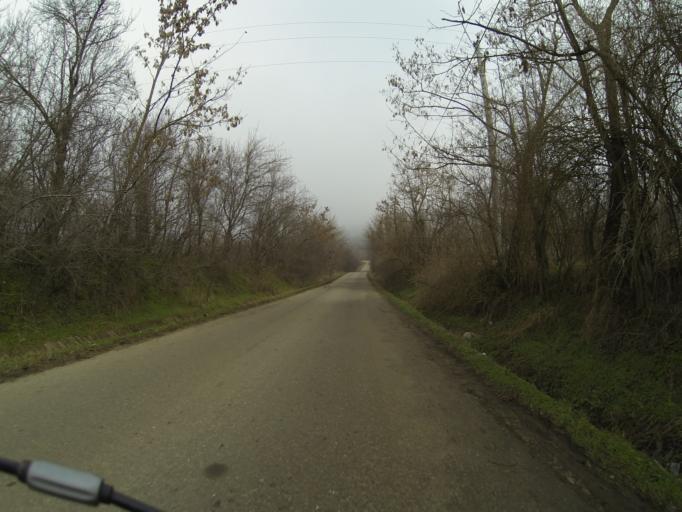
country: RO
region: Mehedinti
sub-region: Comuna Balacita
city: Gvardinita
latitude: 44.3929
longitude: 23.1435
